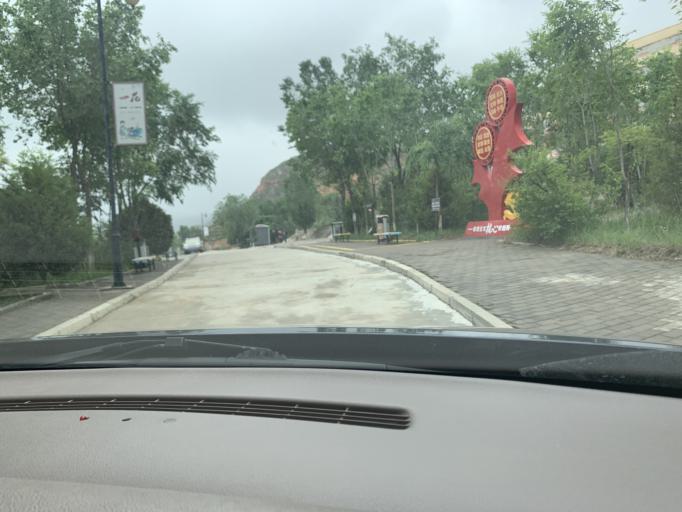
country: CN
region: Gansu Sheng
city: Gulang
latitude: 37.5630
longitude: 102.7427
